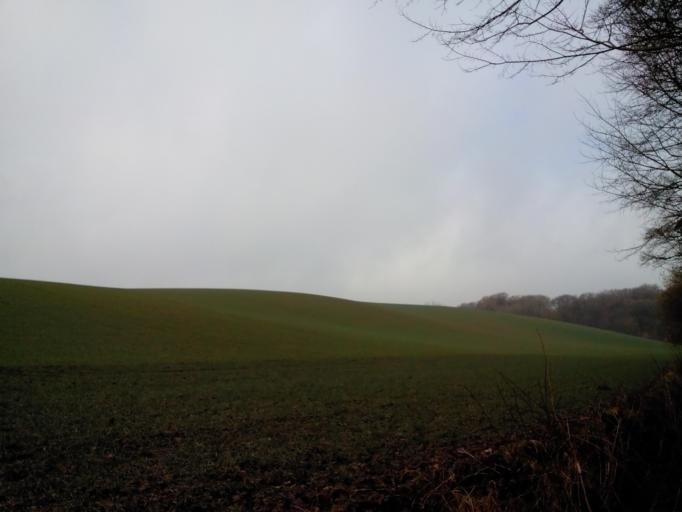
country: BE
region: Wallonia
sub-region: Province du Brabant Wallon
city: Wavre
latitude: 50.7424
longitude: 4.6424
